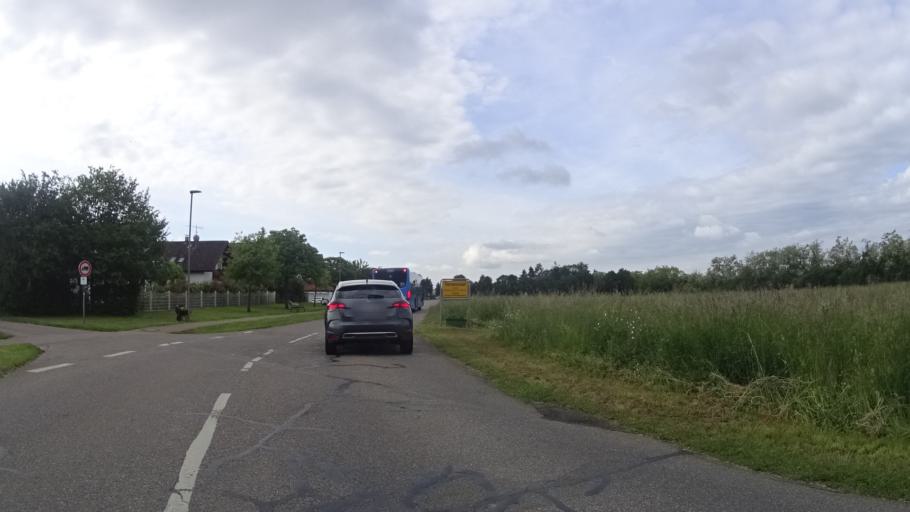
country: DE
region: Baden-Wuerttemberg
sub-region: Freiburg Region
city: Schliengen
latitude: 47.7736
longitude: 7.5529
